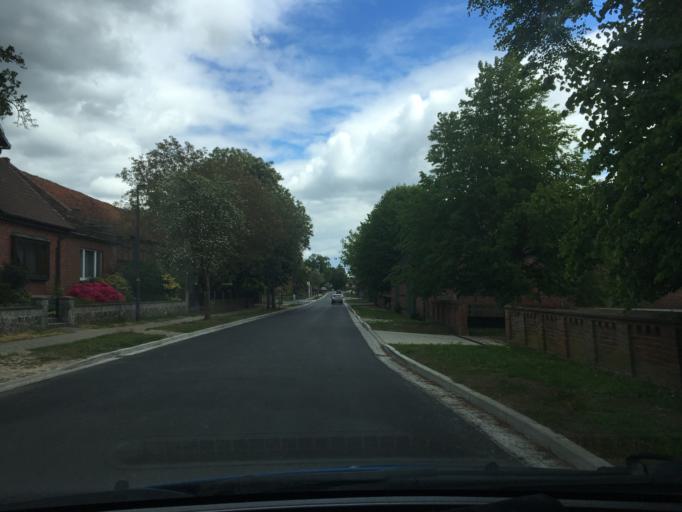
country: DE
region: Lower Saxony
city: Suderburg
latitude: 52.9116
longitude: 10.4811
